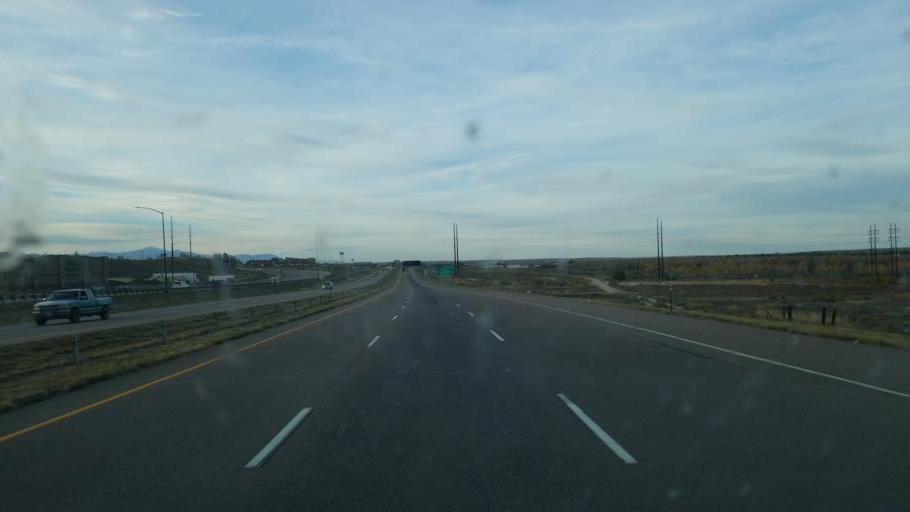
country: US
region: Colorado
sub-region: Pueblo County
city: Pueblo
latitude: 38.3259
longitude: -104.6158
